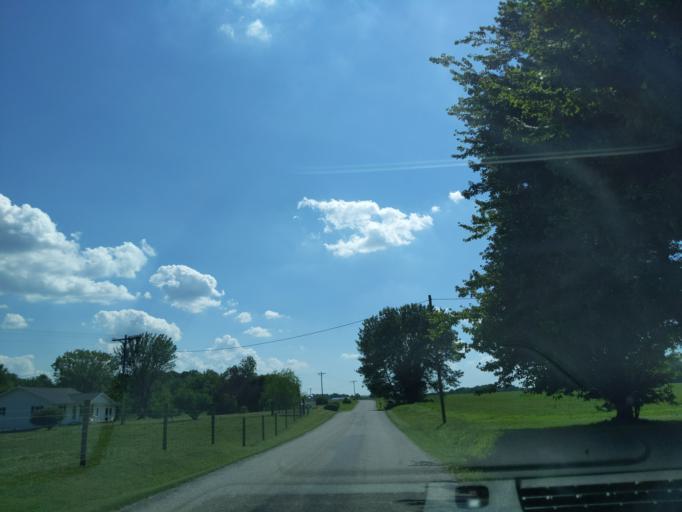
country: US
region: Indiana
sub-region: Ripley County
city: Osgood
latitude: 39.1993
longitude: -85.3801
